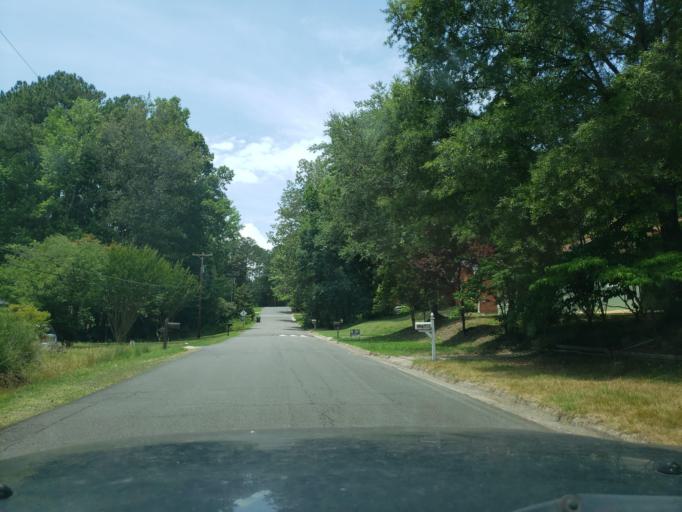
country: US
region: North Carolina
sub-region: Durham County
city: Durham
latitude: 35.9519
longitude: -78.9356
